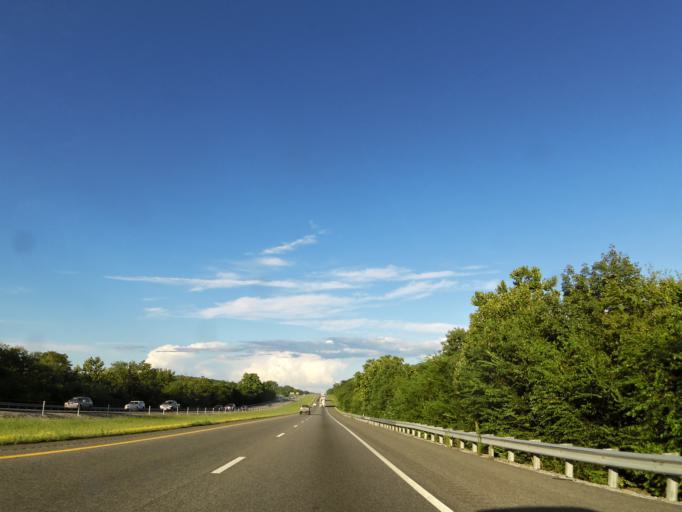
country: US
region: Tennessee
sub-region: Smith County
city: Gordonsville
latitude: 36.1710
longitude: -86.0406
